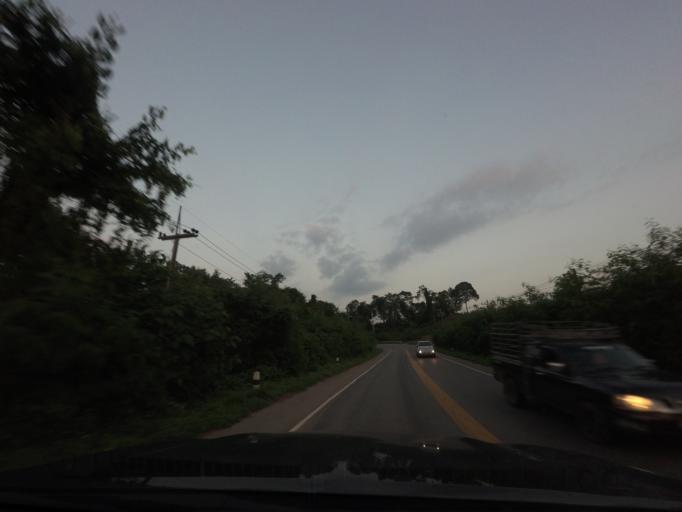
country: TH
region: Nan
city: Na Noi
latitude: 18.4550
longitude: 100.7136
